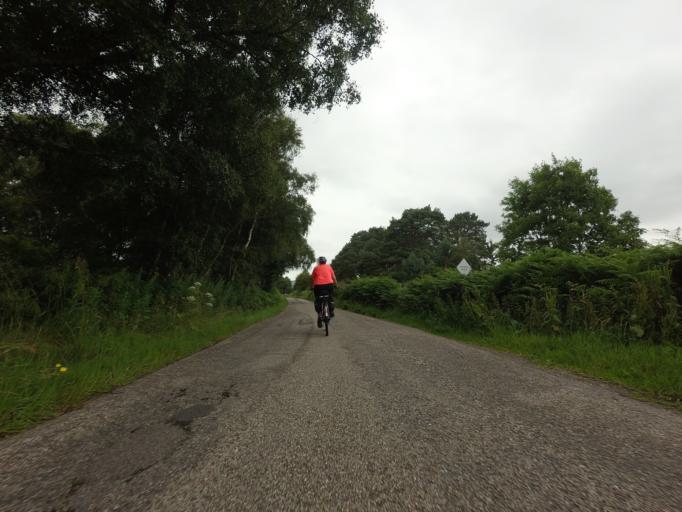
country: GB
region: Scotland
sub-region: Highland
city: Evanton
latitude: 57.9042
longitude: -4.3884
